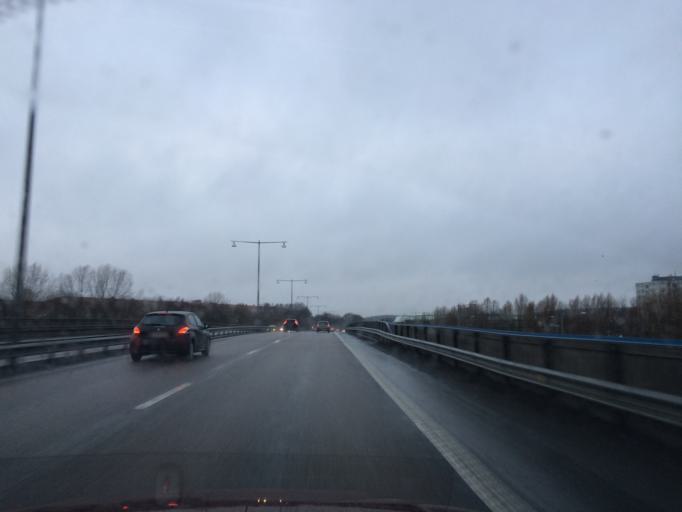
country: SE
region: Vaestra Goetaland
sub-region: Goteborg
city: Majorna
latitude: 57.6520
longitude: 11.9058
